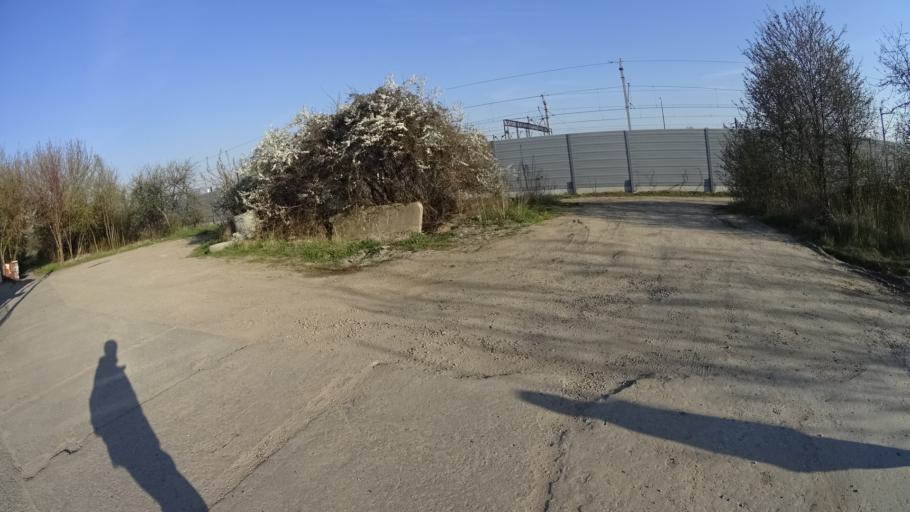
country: PL
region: Masovian Voivodeship
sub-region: Warszawa
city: Ursus
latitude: 52.2159
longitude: 20.9034
